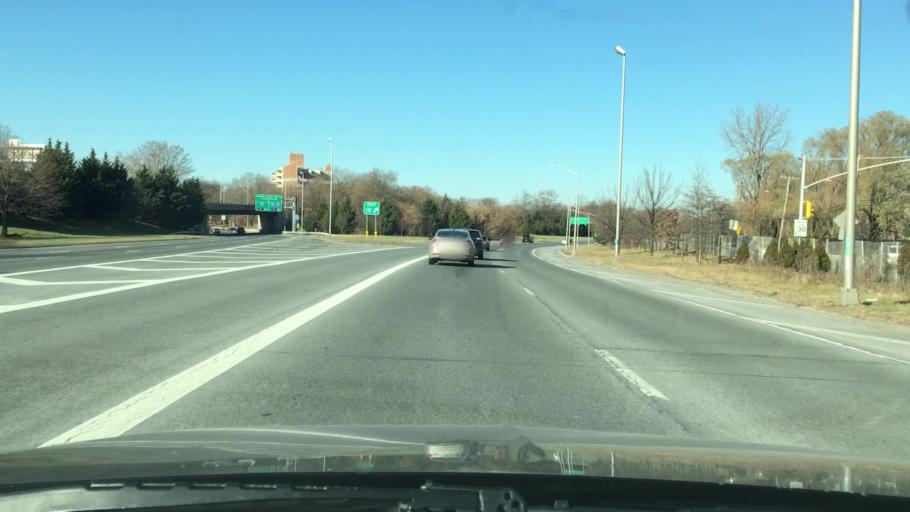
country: US
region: New York
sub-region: Bronx
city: The Bronx
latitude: 40.8205
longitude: -73.8123
